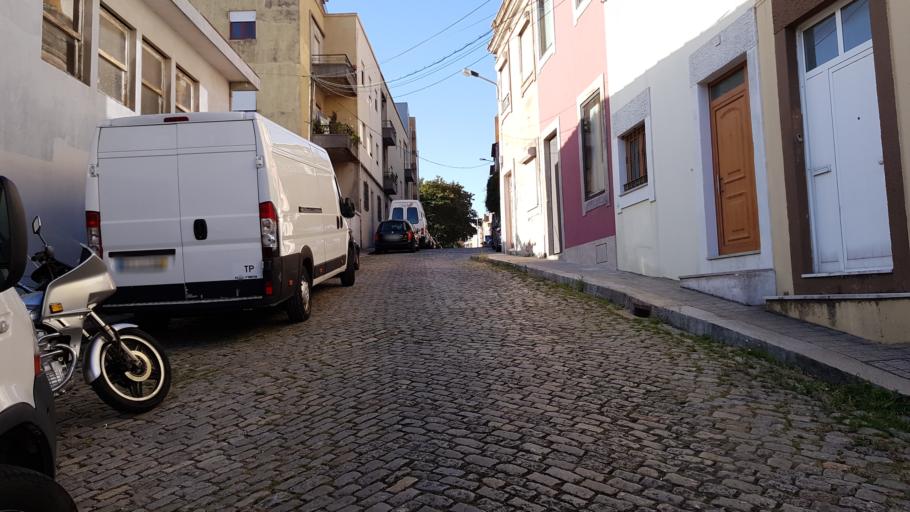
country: PT
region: Porto
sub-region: Porto
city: Porto
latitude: 41.1570
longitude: -8.5984
